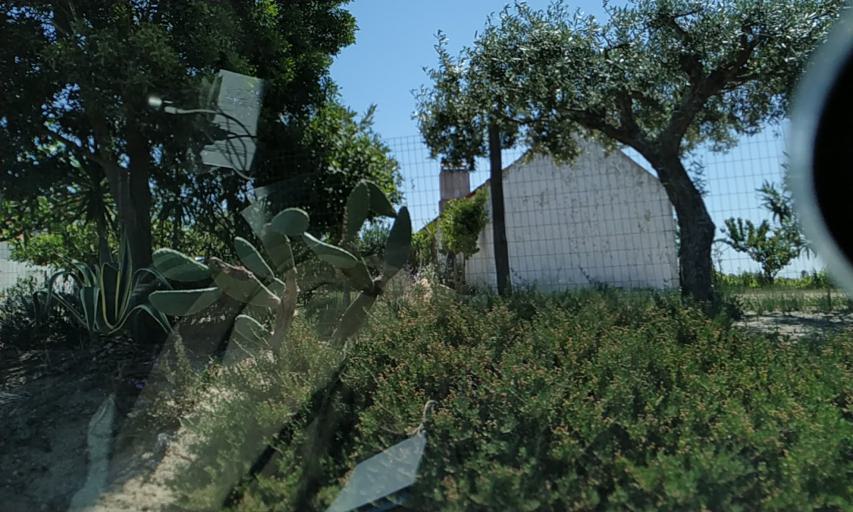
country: PT
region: Setubal
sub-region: Palmela
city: Palmela
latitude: 38.6021
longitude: -8.8075
